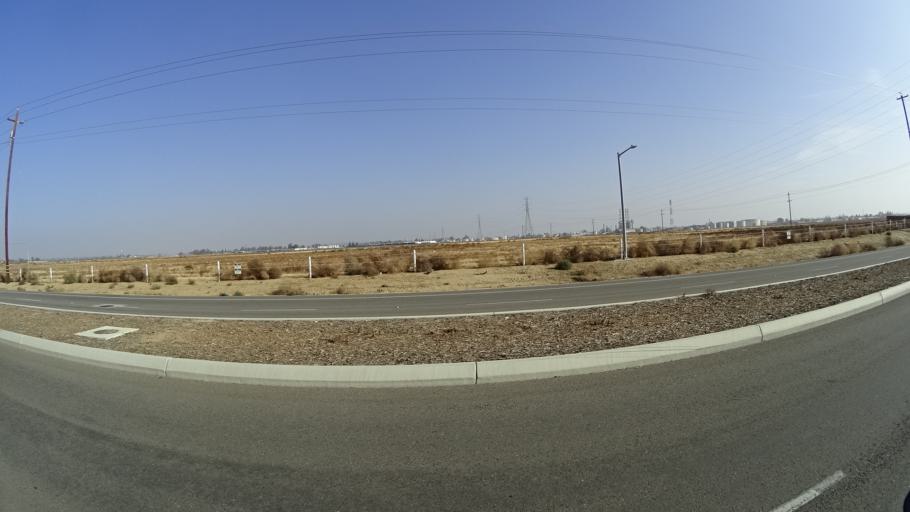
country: US
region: California
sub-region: Kern County
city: Greenacres
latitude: 35.3980
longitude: -119.0651
